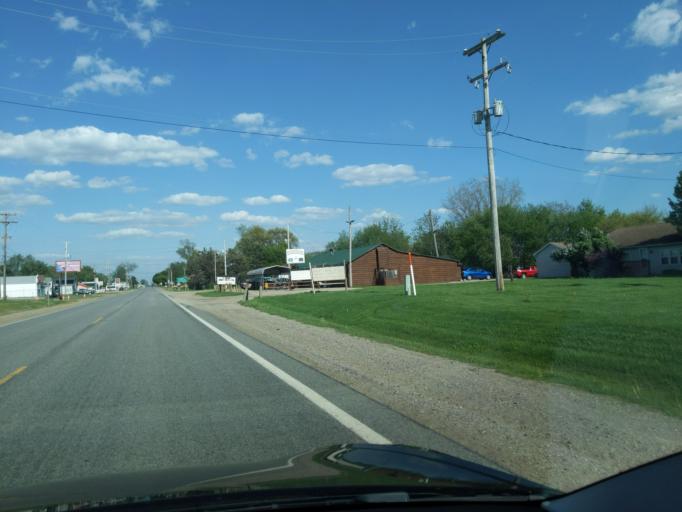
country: US
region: Michigan
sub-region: Ionia County
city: Portland
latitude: 42.7556
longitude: -84.9004
